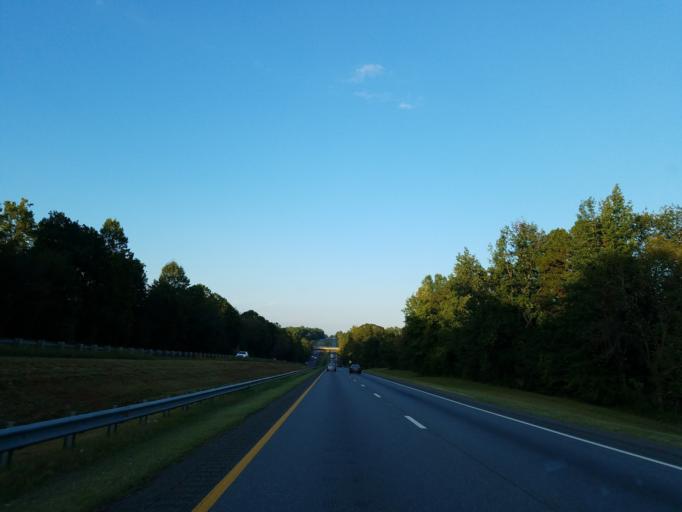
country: US
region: North Carolina
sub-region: Cleveland County
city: Kings Mountain
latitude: 35.2079
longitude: -81.3569
